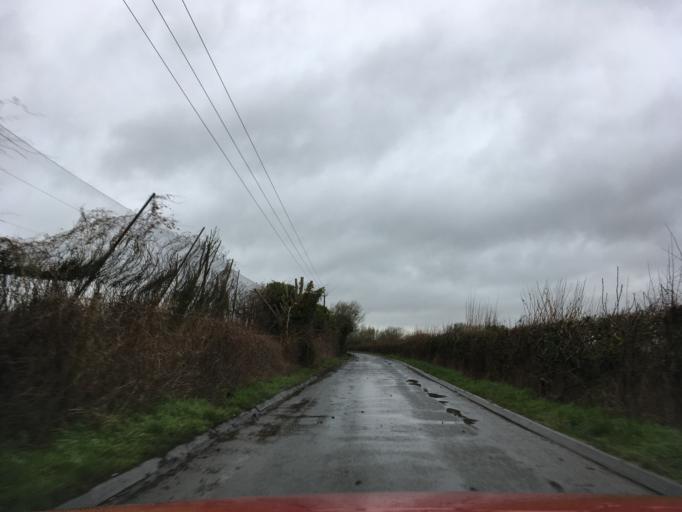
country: GB
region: England
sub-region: Oxfordshire
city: Oxford
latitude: 51.7568
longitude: -1.2836
